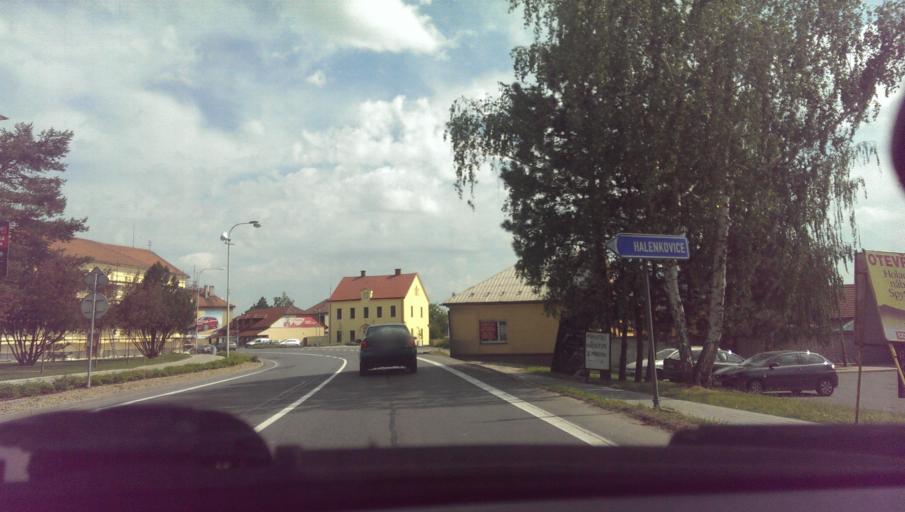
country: CZ
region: Zlin
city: Spytihnev
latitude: 49.1400
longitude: 17.4973
